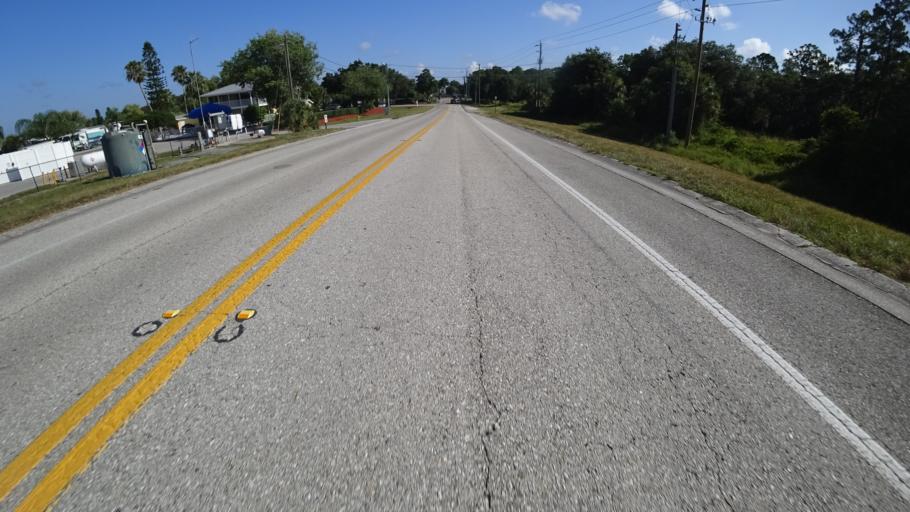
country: US
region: Florida
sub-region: Manatee County
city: Ellenton
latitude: 27.5043
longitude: -82.4814
